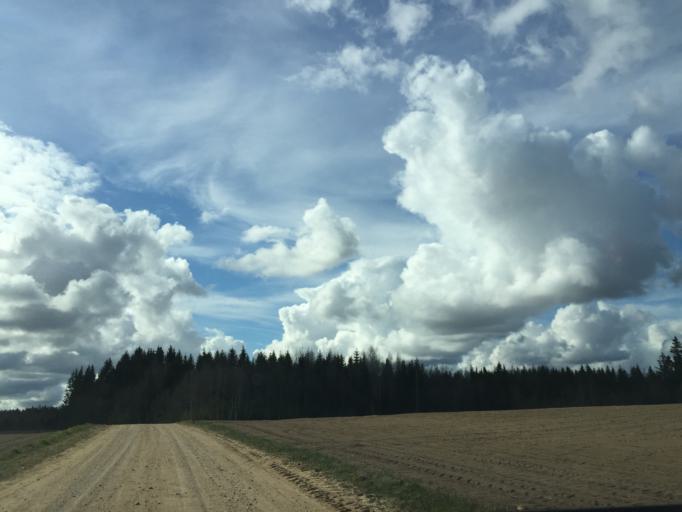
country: LV
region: Burtnieki
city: Matisi
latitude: 57.6130
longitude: 25.0154
